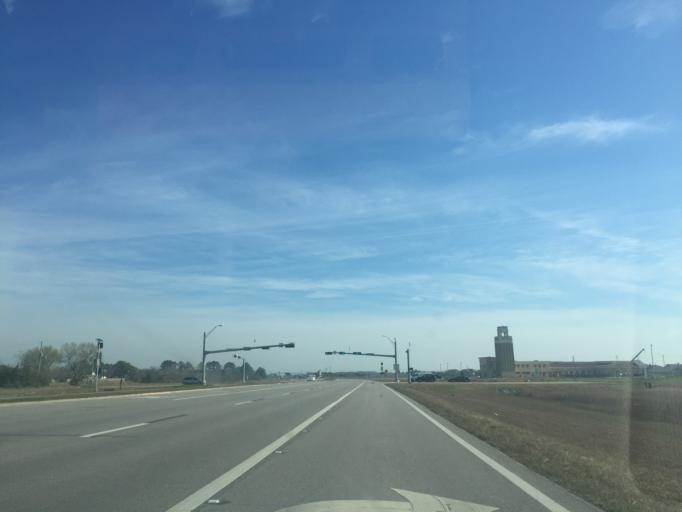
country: US
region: Texas
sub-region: Galveston County
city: Kemah
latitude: 29.5142
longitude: -95.0292
